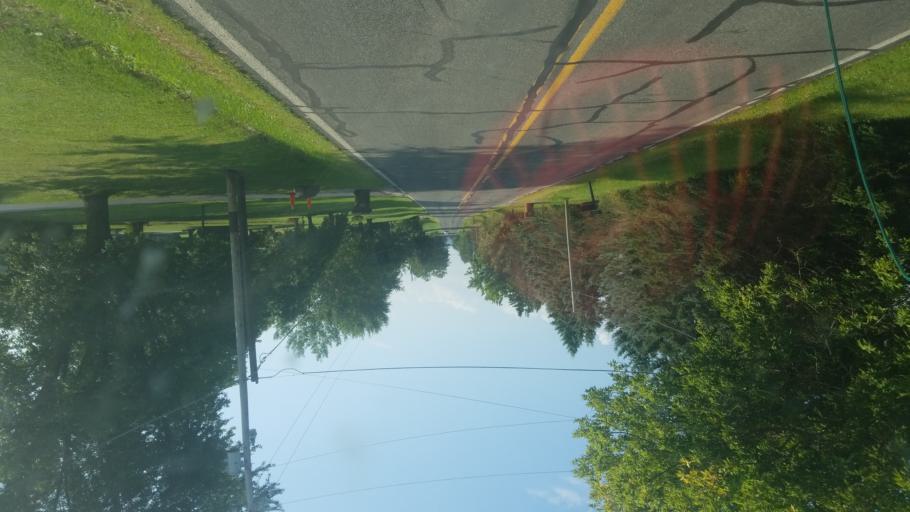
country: US
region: Ohio
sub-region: Medina County
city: Westfield Center
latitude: 41.0251
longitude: -81.9665
